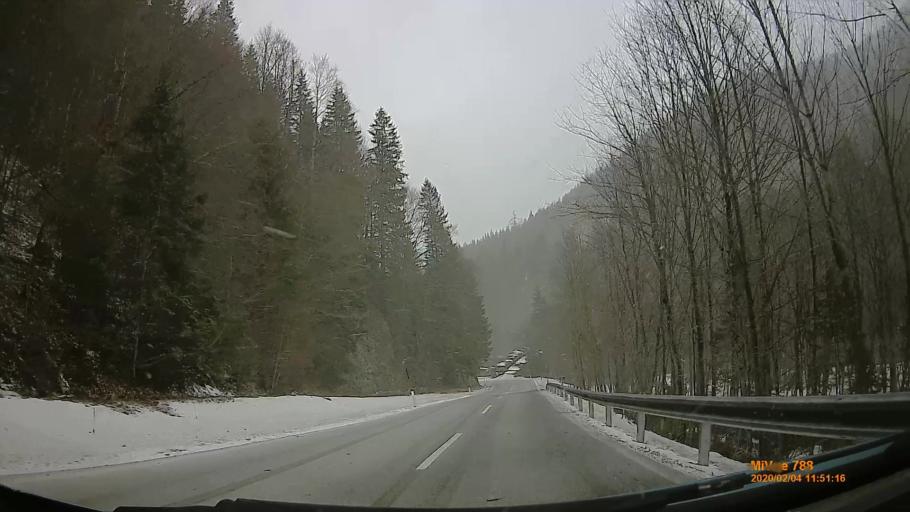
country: AT
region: Styria
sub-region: Politischer Bezirk Bruck-Muerzzuschlag
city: Muerzsteg
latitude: 47.7370
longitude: 15.4854
